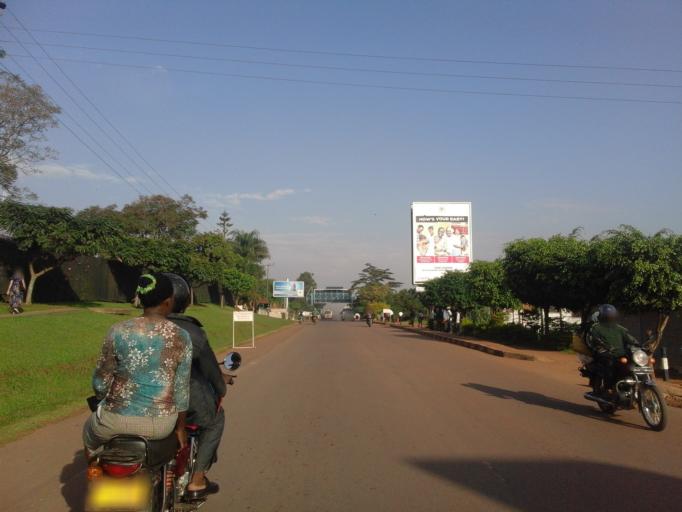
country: UG
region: Central Region
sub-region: Kampala District
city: Kampala
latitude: 0.3008
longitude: 32.5926
